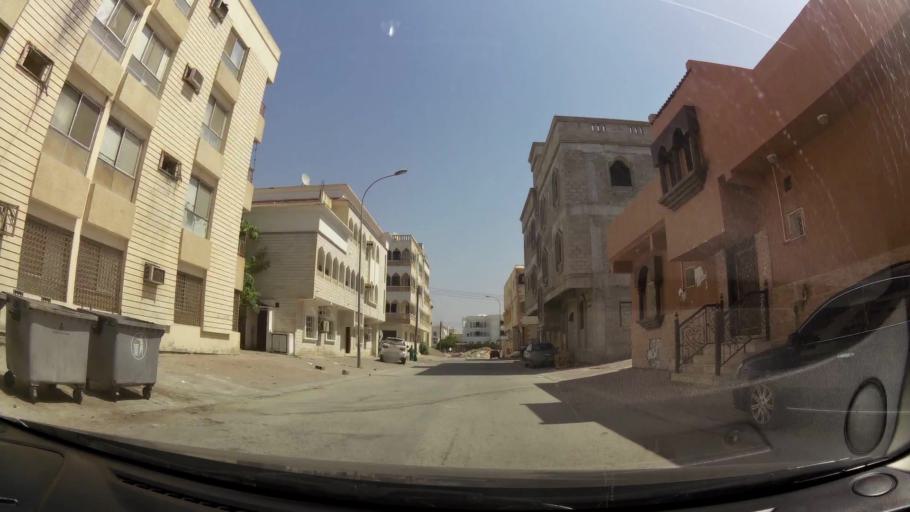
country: OM
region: Zufar
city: Salalah
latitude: 17.0203
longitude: 54.1083
